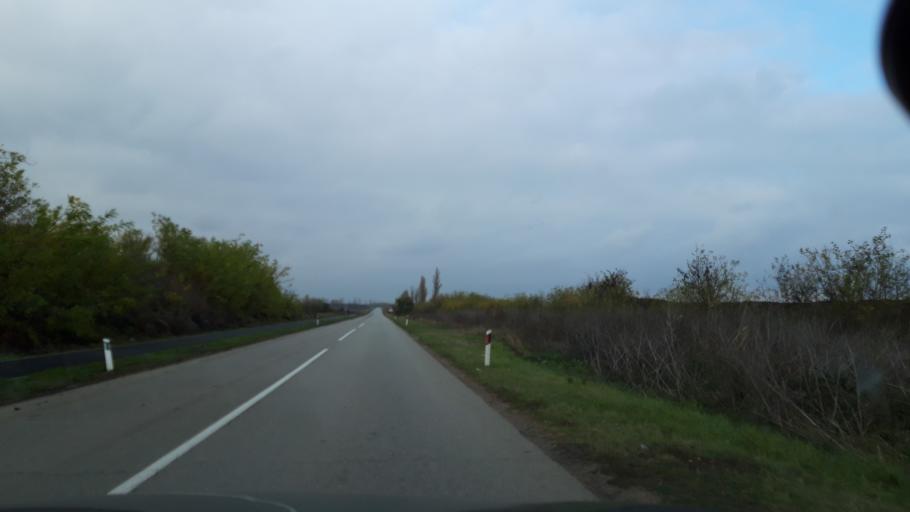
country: RS
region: Autonomna Pokrajina Vojvodina
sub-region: Severnobanatski Okrug
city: Novi Knezevac
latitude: 46.0654
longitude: 20.1034
